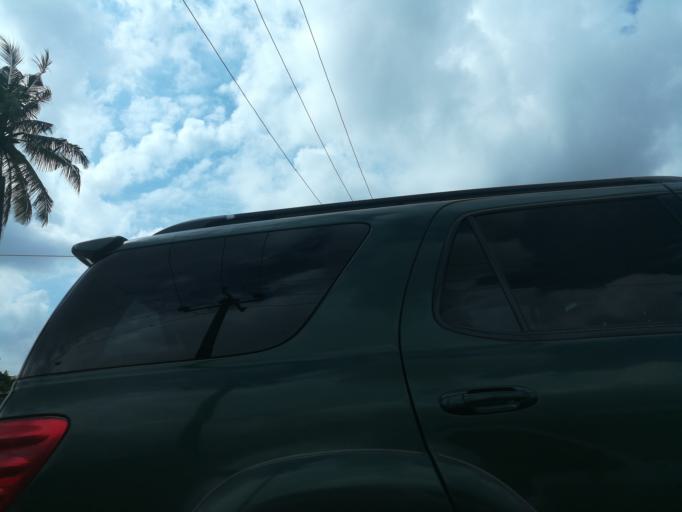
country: NG
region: Lagos
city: Mushin
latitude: 6.5448
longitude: 3.3577
